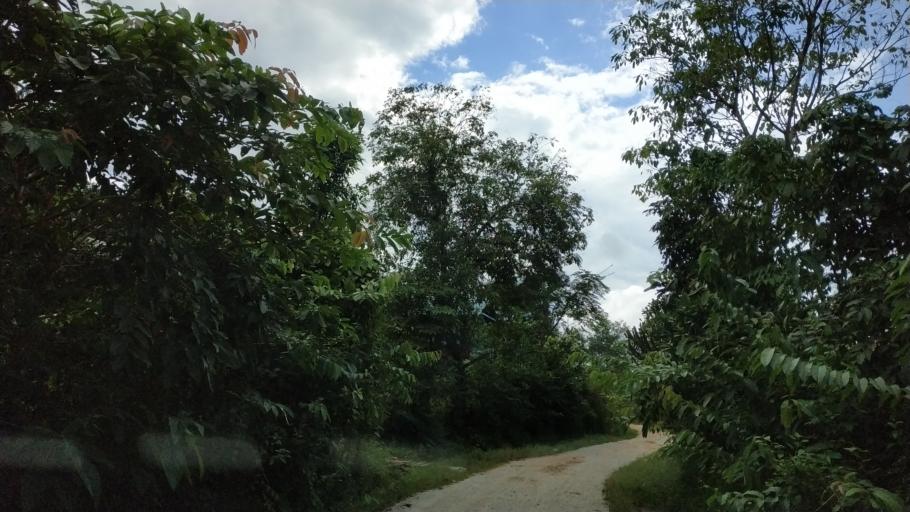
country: MM
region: Tanintharyi
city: Dawei
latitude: 14.1871
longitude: 98.1654
